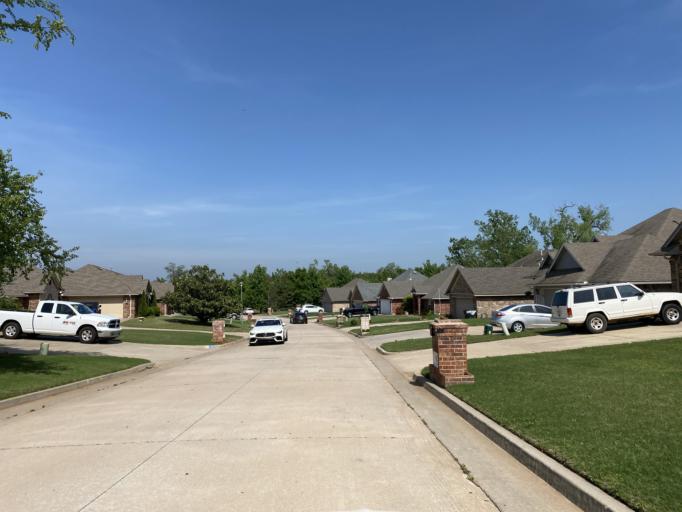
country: US
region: Oklahoma
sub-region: Oklahoma County
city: Nicoma Park
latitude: 35.4716
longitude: -97.3377
